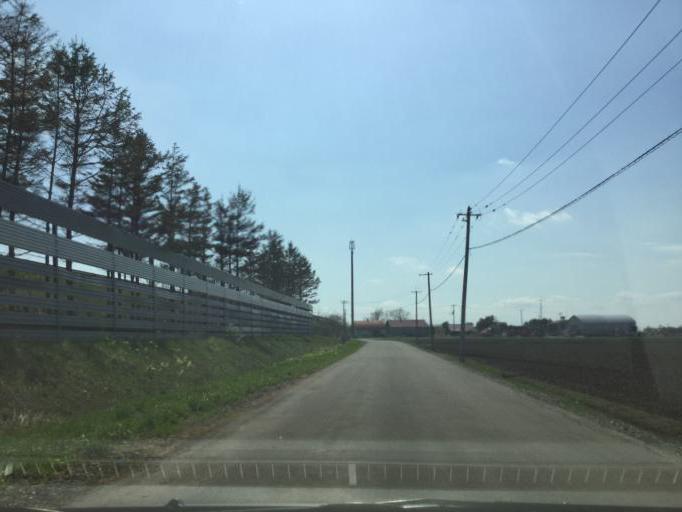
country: JP
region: Hokkaido
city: Iwamizawa
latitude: 43.1503
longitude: 141.6992
